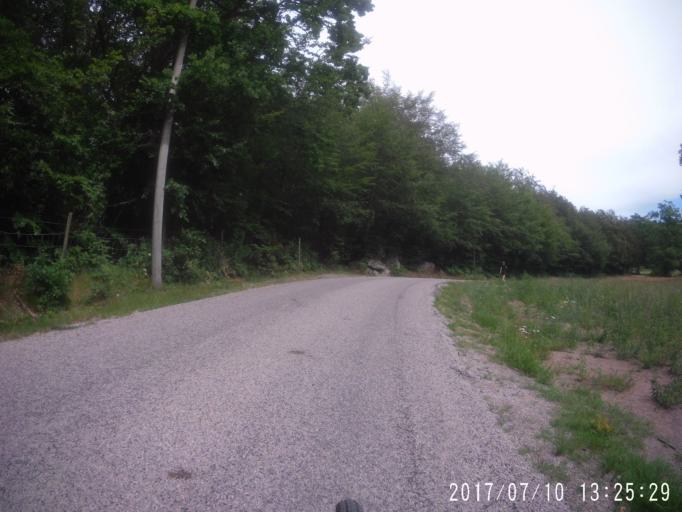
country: SE
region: Blekinge
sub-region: Ronneby Kommun
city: Brakne-Hoby
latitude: 56.1610
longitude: 15.0697
